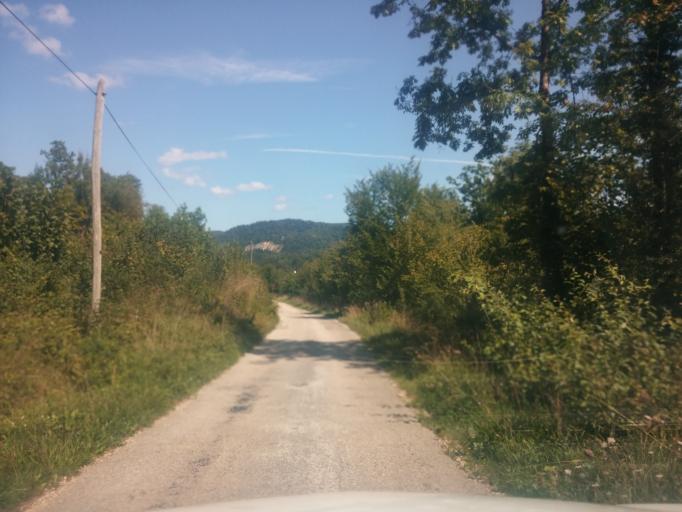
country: FR
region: Franche-Comte
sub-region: Departement du Jura
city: Saint-Lupicin
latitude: 46.4102
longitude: 5.7930
